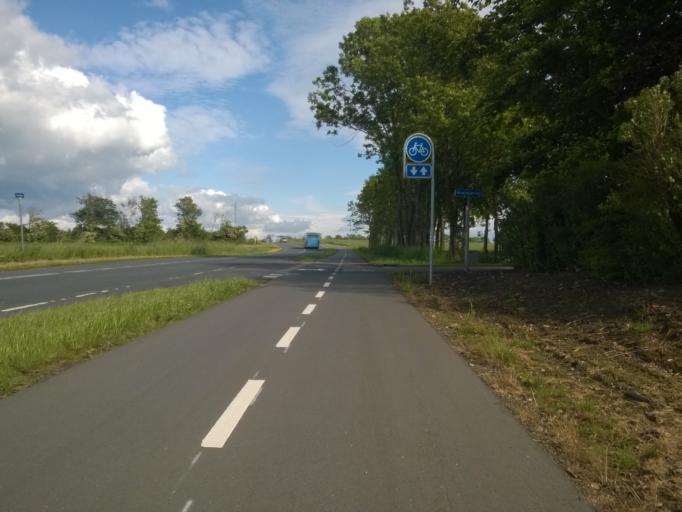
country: DK
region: Central Jutland
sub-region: Holstebro Kommune
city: Vinderup
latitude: 56.4626
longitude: 8.8487
